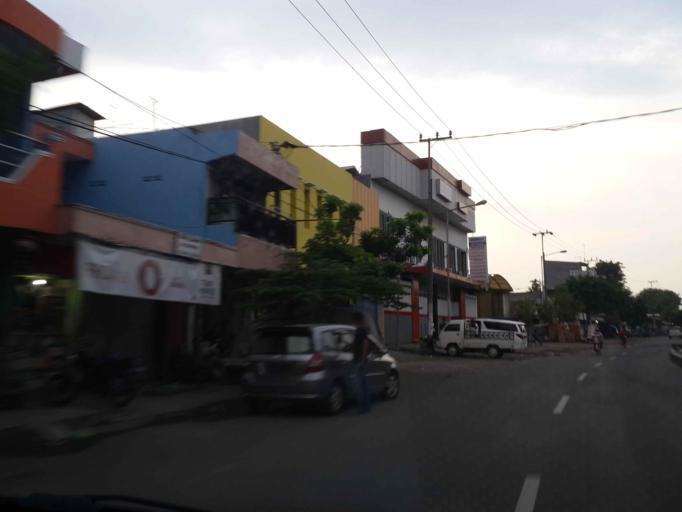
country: ID
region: East Java
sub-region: Kota Surabaya
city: Surabaya
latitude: -7.2546
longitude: 112.7280
